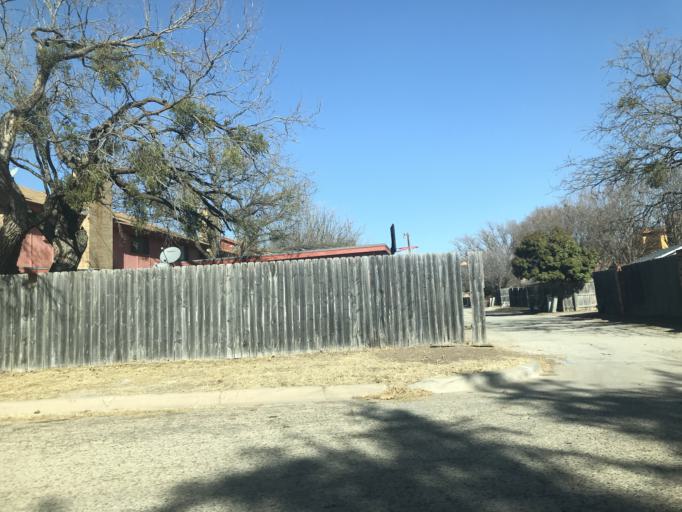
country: US
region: Texas
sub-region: Taylor County
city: Abilene
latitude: 32.4579
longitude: -99.7024
